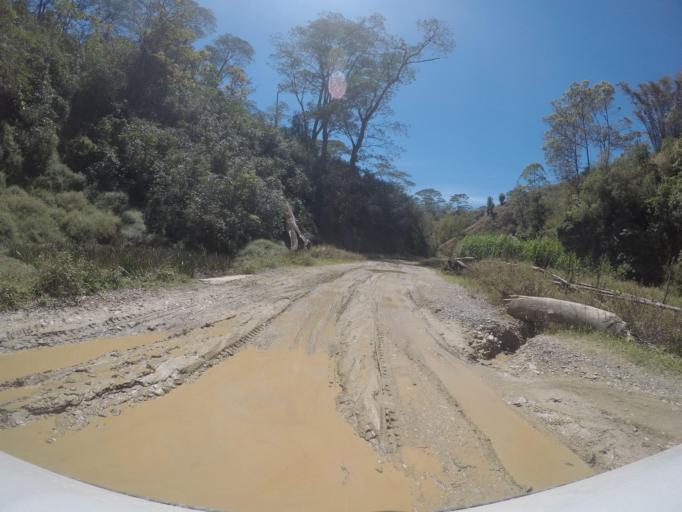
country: TL
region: Ermera
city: Gleno
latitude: -8.7763
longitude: 125.3861
